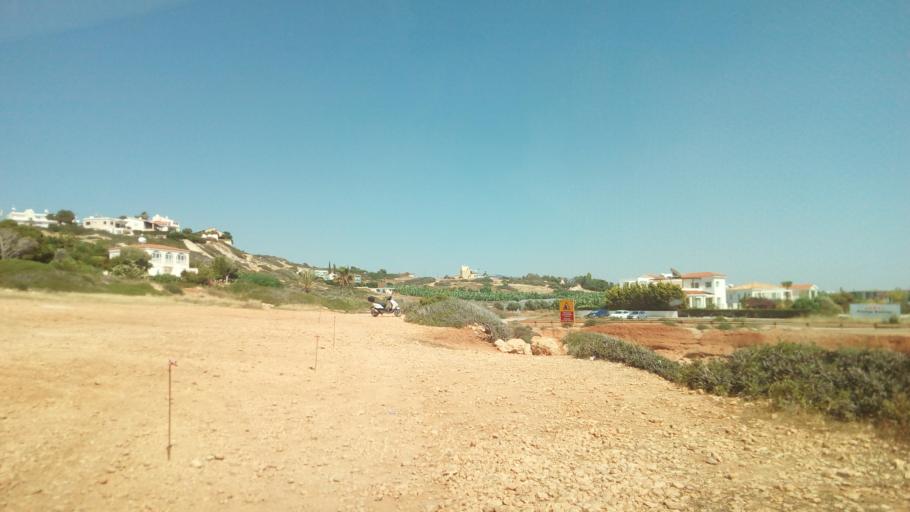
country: CY
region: Pafos
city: Pegeia
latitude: 34.8845
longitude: 32.3326
